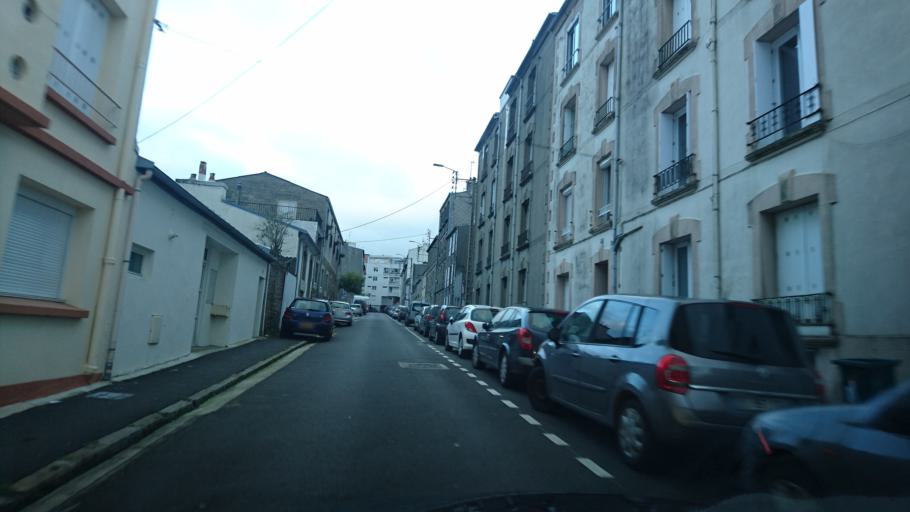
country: FR
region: Brittany
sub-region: Departement du Finistere
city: Brest
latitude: 48.3956
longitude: -4.4715
